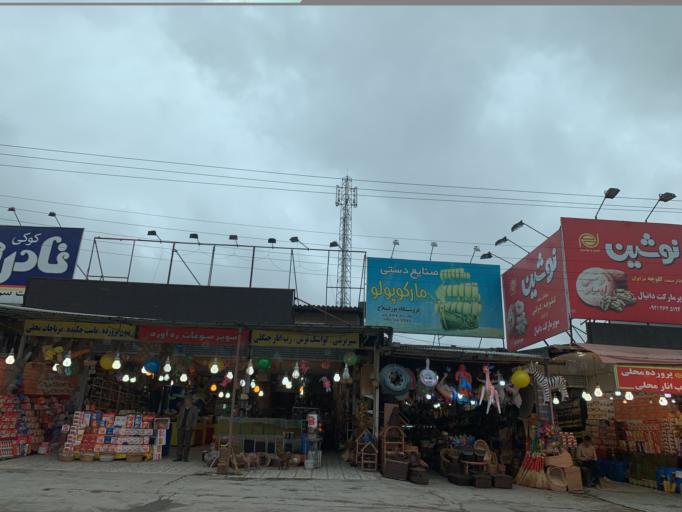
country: IR
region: Mazandaran
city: Amol
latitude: 36.4649
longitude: 52.3943
